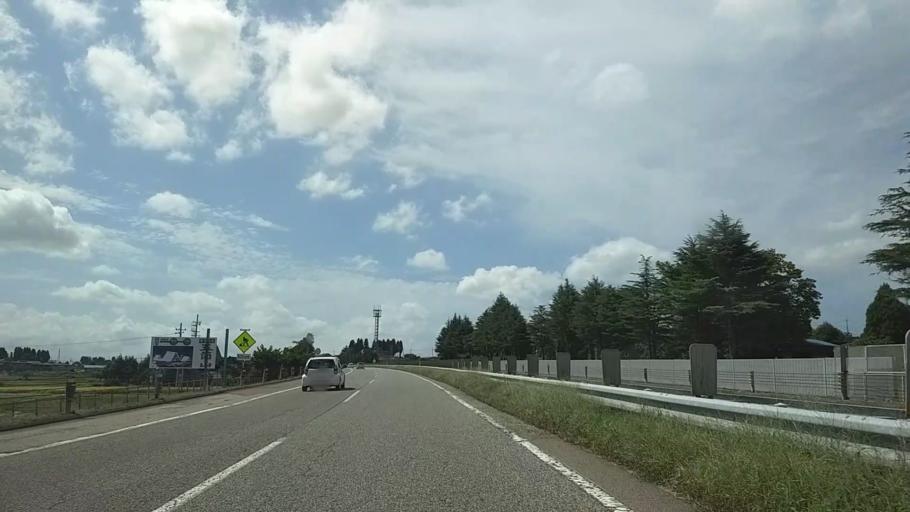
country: JP
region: Toyama
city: Takaoka
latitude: 36.6803
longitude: 137.0412
